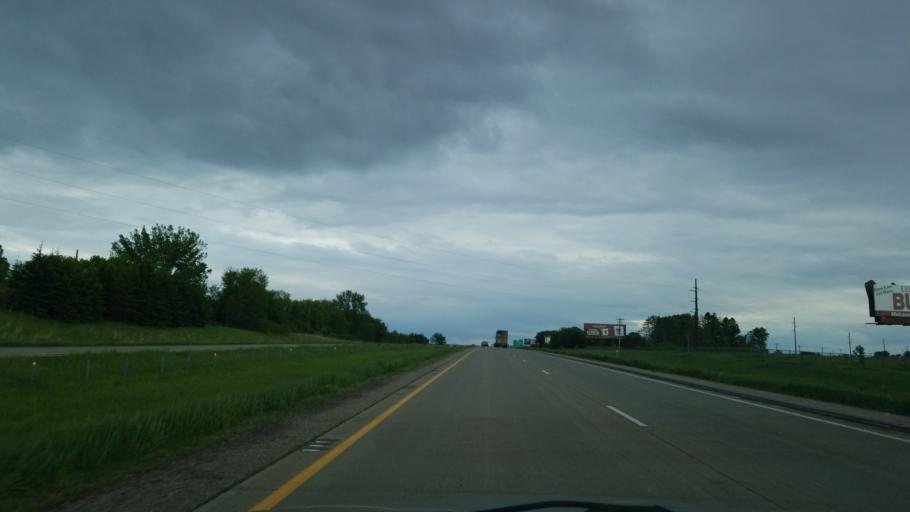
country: US
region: Minnesota
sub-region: Stearns County
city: Sauk Centre
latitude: 45.7352
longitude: -94.9757
